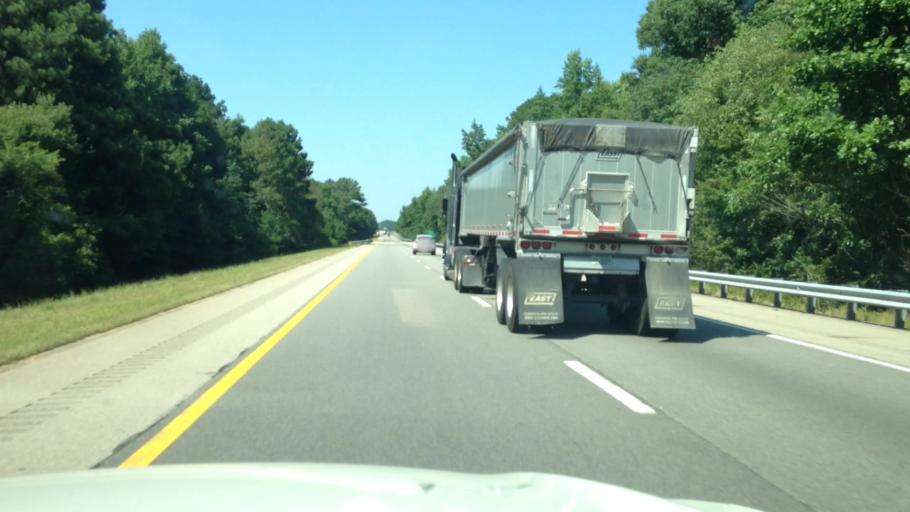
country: US
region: North Carolina
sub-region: Wilson County
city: Lucama
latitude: 35.6895
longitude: -78.0544
